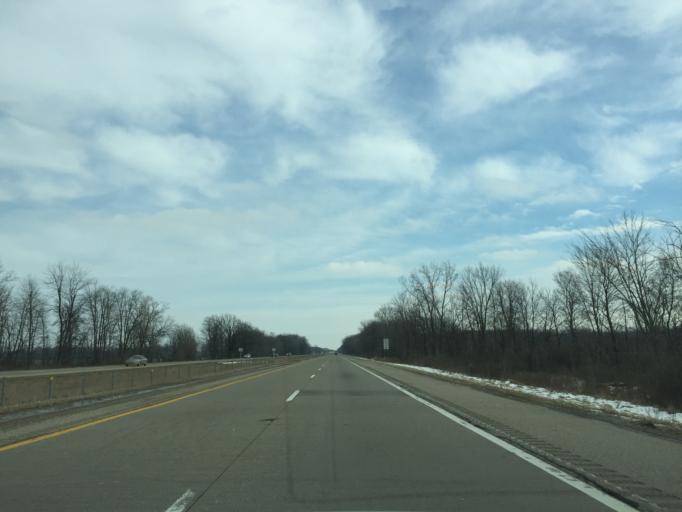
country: US
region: Michigan
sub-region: Ionia County
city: Saranac
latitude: 42.8792
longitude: -85.2322
